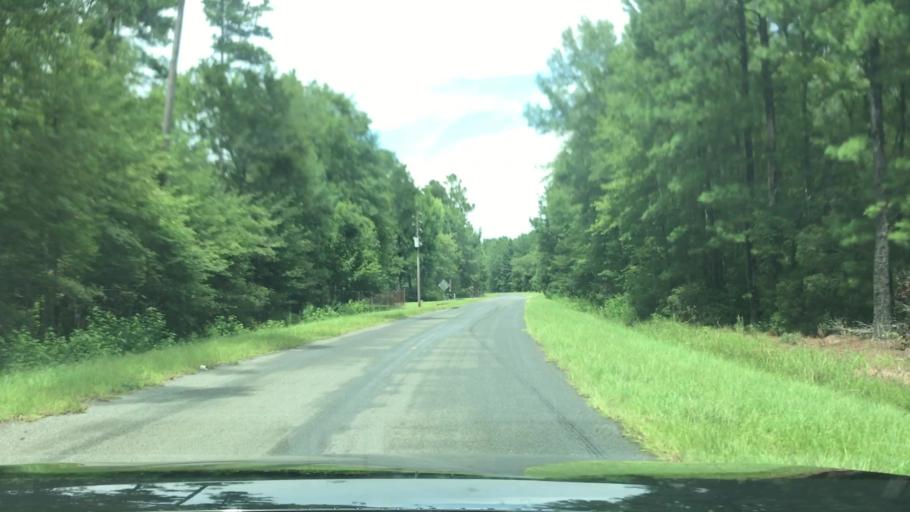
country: US
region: South Carolina
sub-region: Colleton County
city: Walterboro
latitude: 33.0039
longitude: -80.6713
